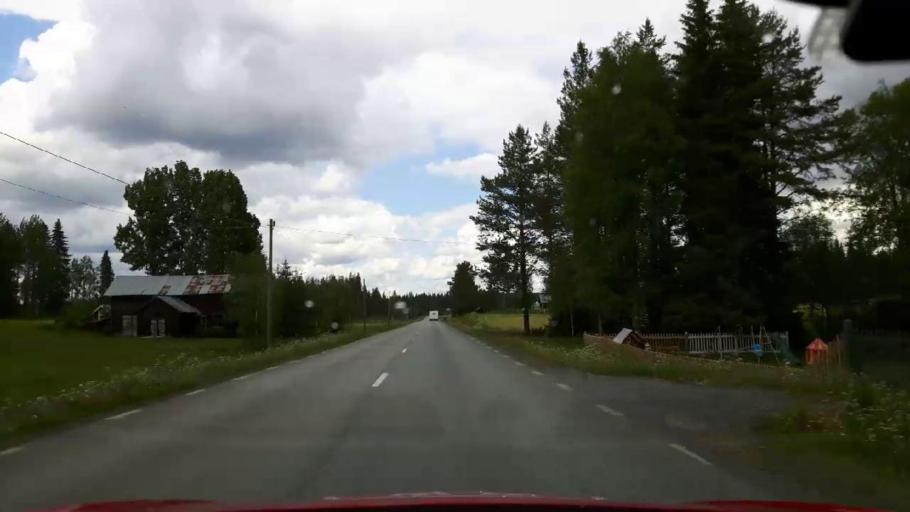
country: SE
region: Jaemtland
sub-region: Krokoms Kommun
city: Krokom
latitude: 63.5194
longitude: 14.2325
